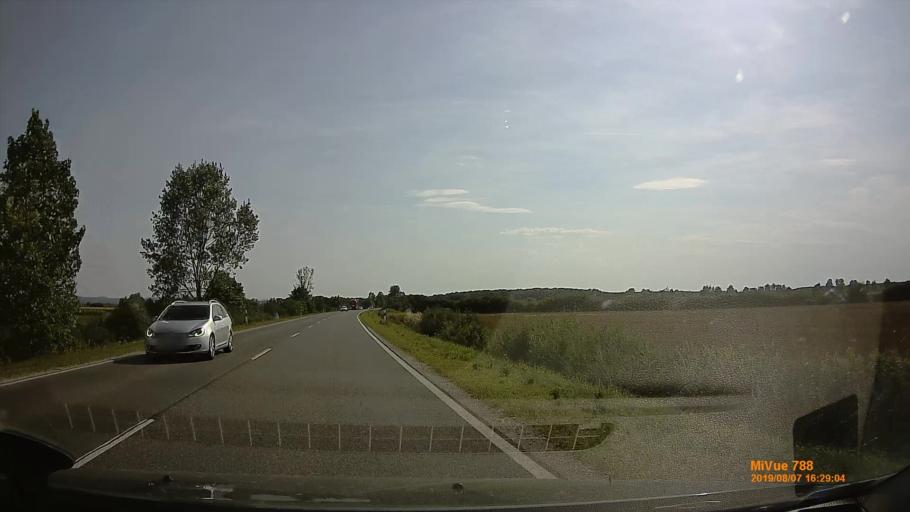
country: HU
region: Zala
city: Lenti
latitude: 46.6859
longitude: 16.5345
